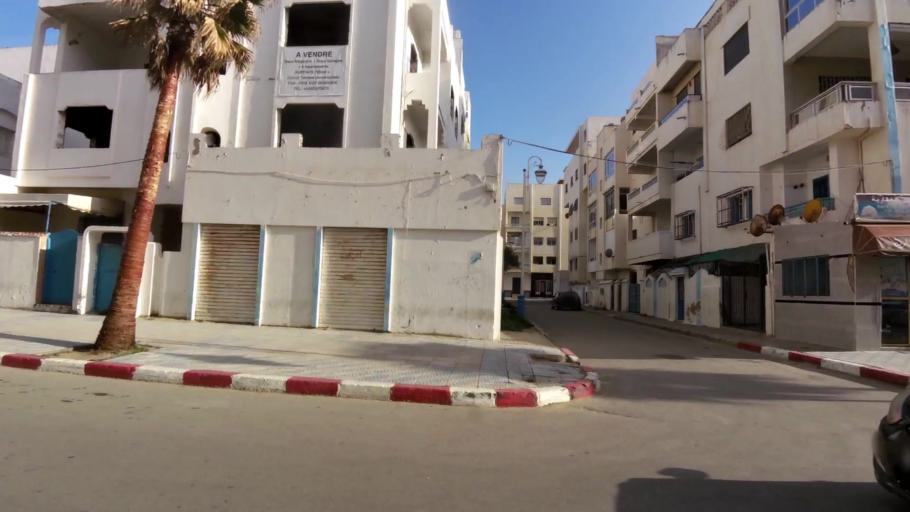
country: MA
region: Tanger-Tetouan
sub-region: Tetouan
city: Martil
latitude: 35.6218
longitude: -5.2730
